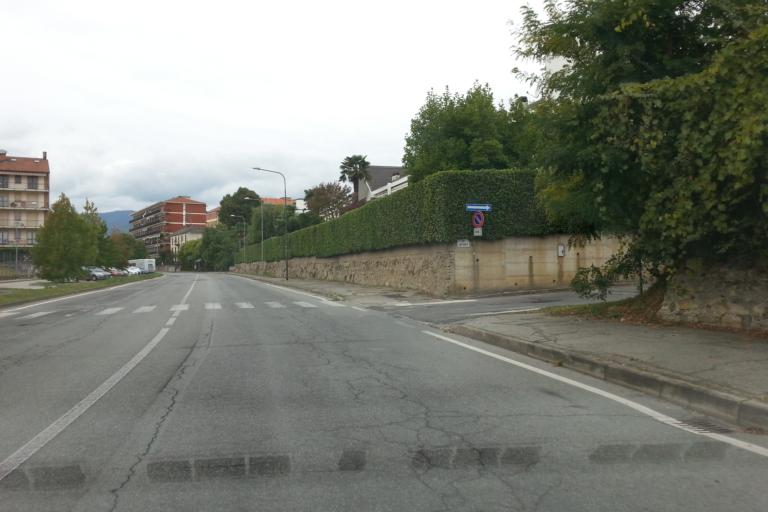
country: IT
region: Piedmont
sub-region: Provincia di Torino
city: Pinerolo
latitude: 44.8928
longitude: 7.3487
